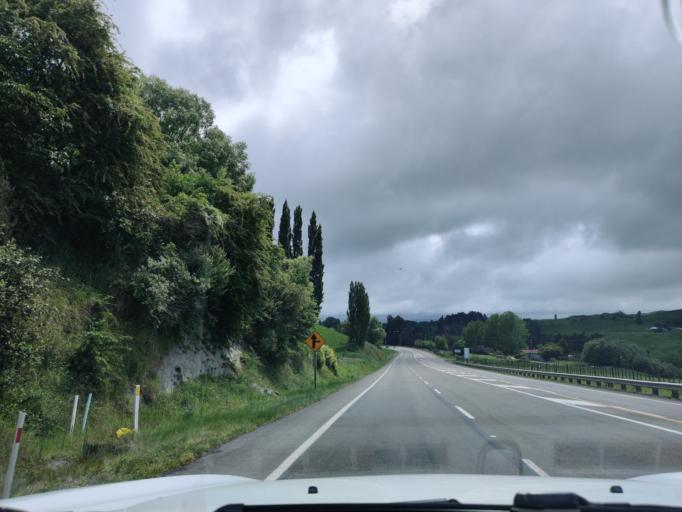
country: NZ
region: Manawatu-Wanganui
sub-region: Ruapehu District
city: Waiouru
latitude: -39.6623
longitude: 175.7817
